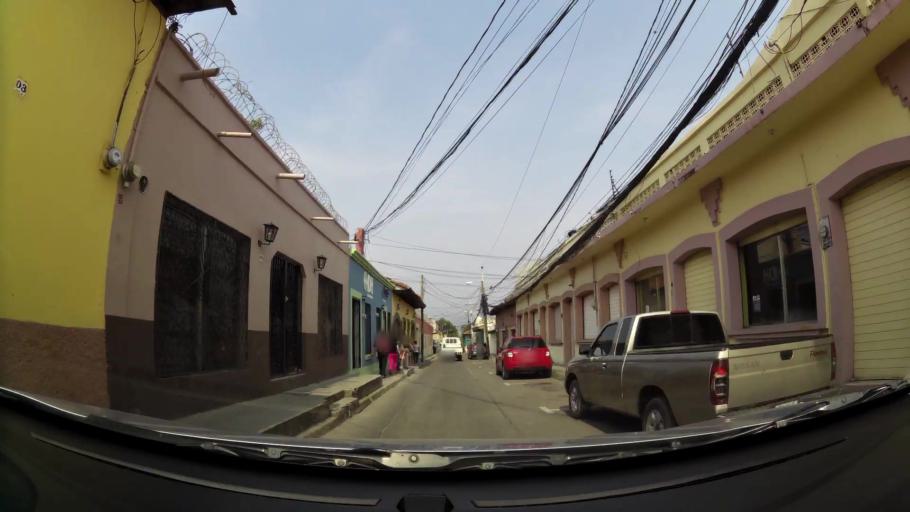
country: HN
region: Comayagua
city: Comayagua
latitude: 14.4603
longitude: -87.6429
